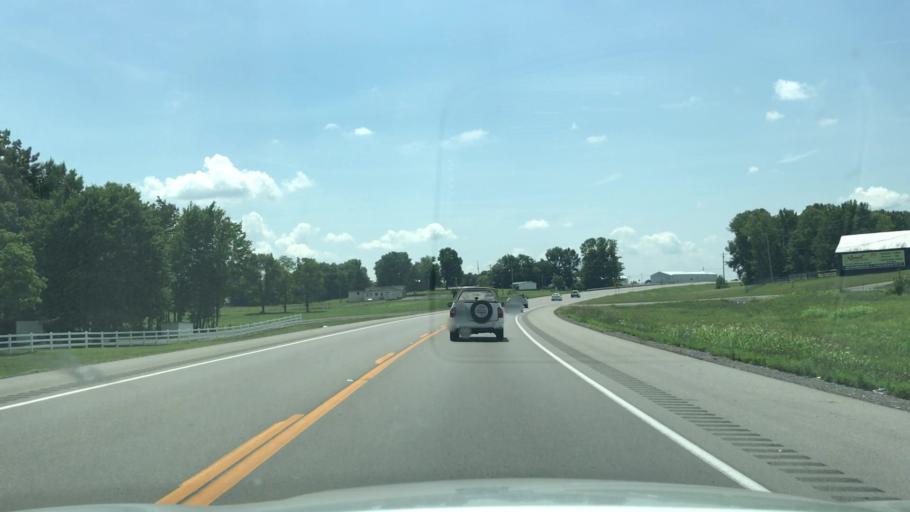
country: US
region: Tennessee
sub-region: Pickett County
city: Byrdstown
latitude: 36.6263
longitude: -85.0897
